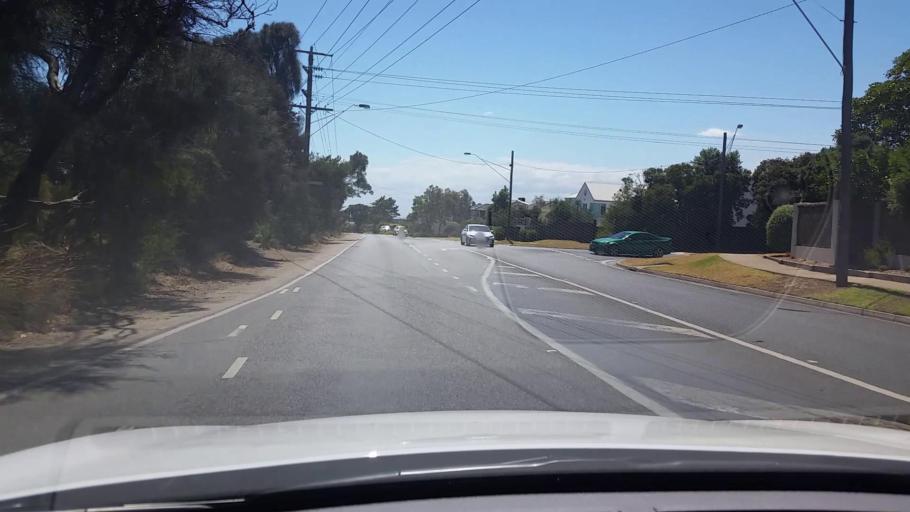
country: AU
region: Victoria
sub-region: Mornington Peninsula
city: Mount Martha
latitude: -38.2437
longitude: 145.0299
